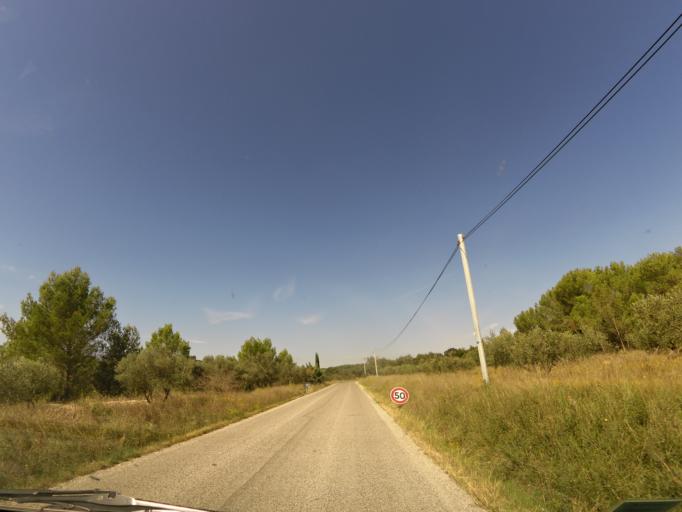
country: FR
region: Languedoc-Roussillon
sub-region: Departement du Gard
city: Uchaud
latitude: 43.7627
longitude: 4.2554
